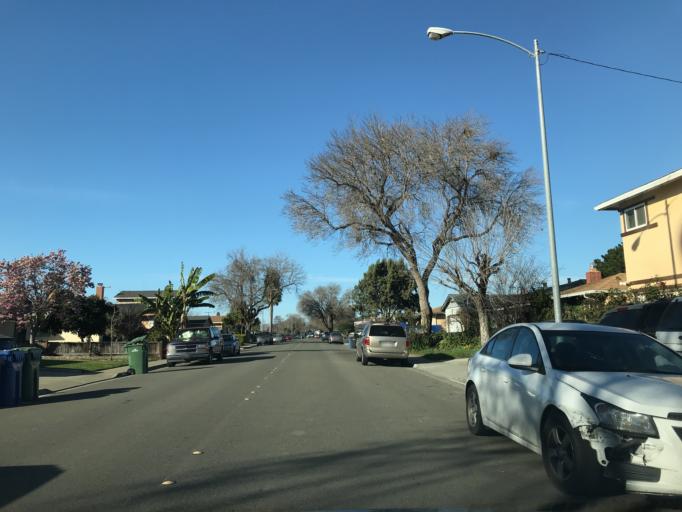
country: US
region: California
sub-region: Santa Clara County
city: Milpitas
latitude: 37.4316
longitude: -121.9166
